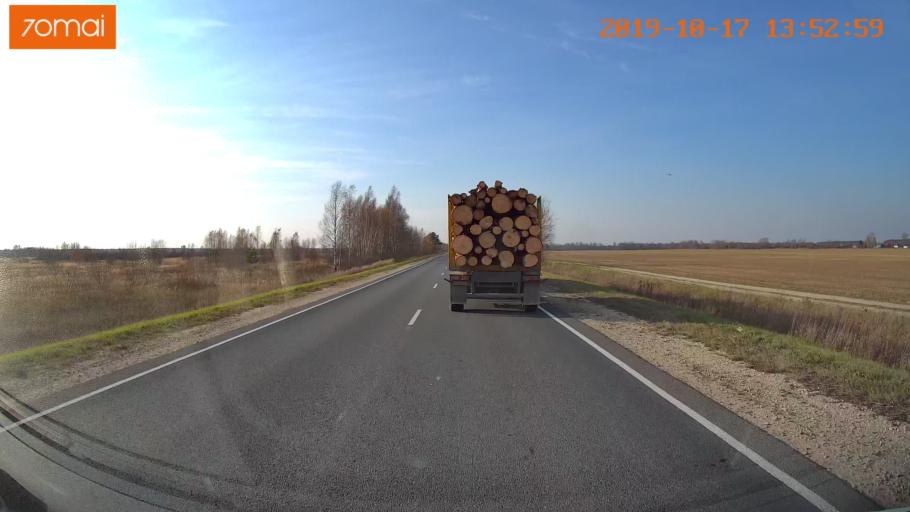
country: RU
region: Rjazan
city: Spas-Klepiki
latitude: 55.1416
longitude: 40.3504
